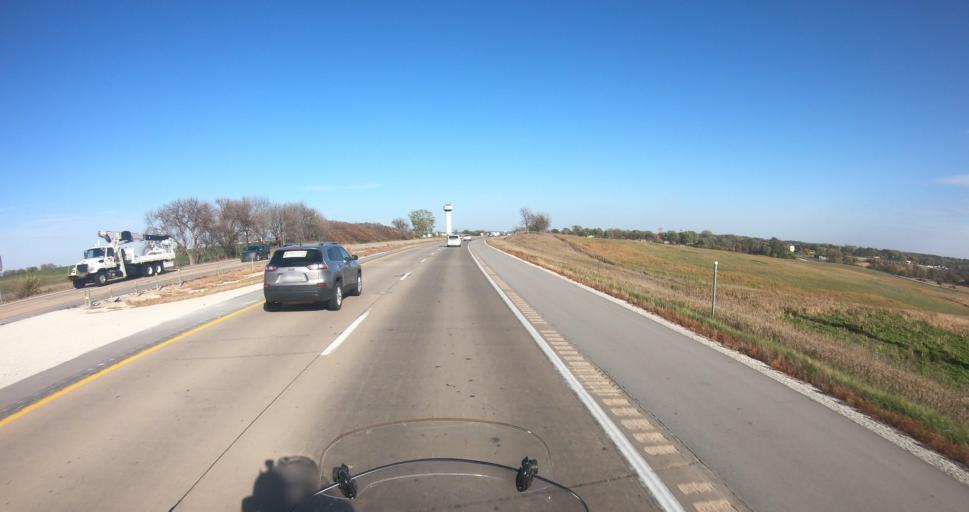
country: US
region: Iowa
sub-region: Dallas County
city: De Soto
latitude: 41.5386
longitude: -94.0254
